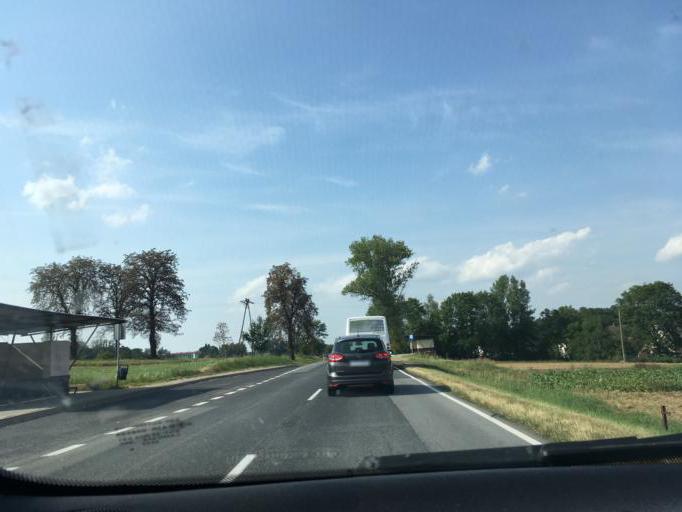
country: PL
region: Opole Voivodeship
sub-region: Powiat prudnicki
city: Laka Prudnicka
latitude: 50.3756
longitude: 17.5343
